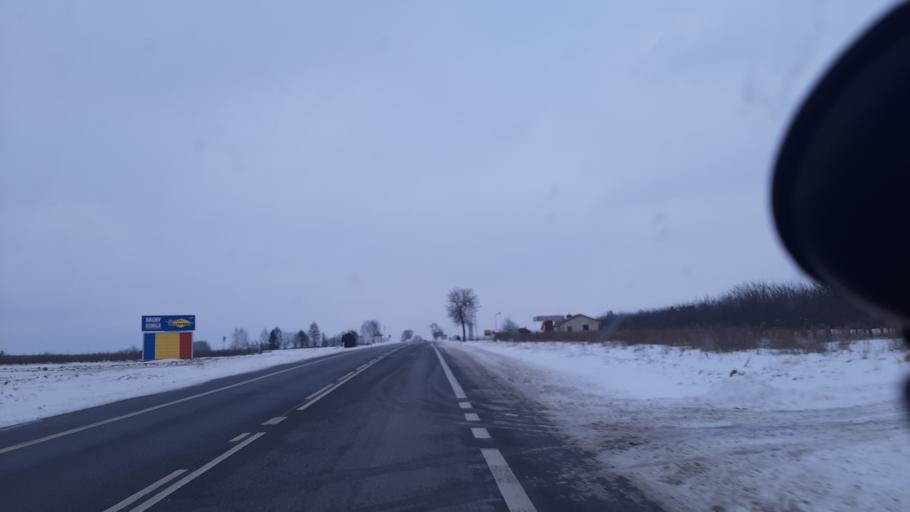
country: PL
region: Lublin Voivodeship
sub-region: Powiat pulawski
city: Markuszow
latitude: 51.3828
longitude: 22.2239
